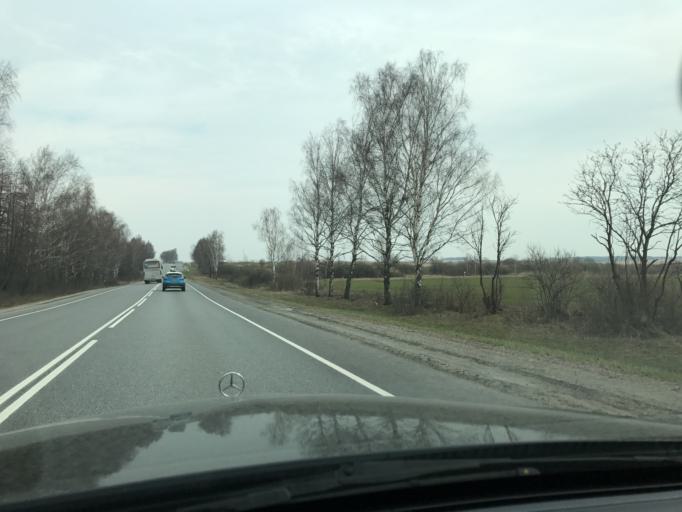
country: RU
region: Vladimir
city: Bogolyubovo
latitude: 56.2942
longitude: 40.4692
